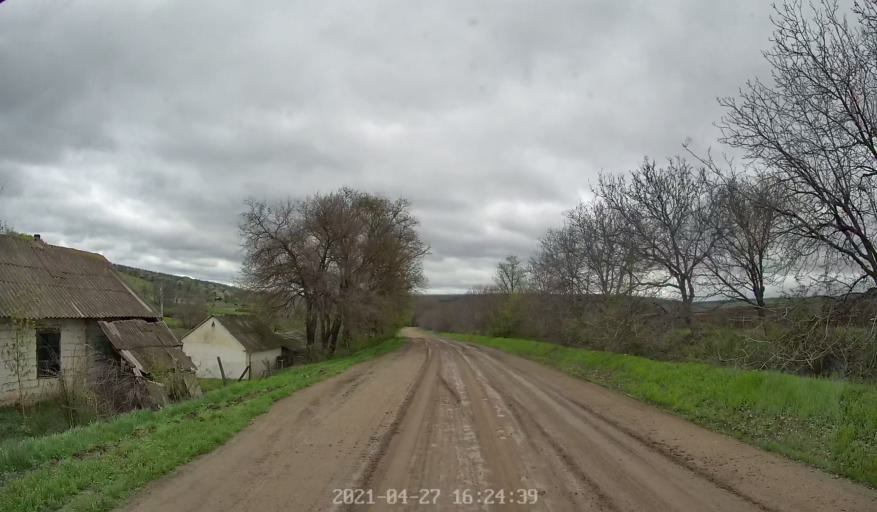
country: MD
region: Chisinau
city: Singera
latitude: 46.9903
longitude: 29.0209
